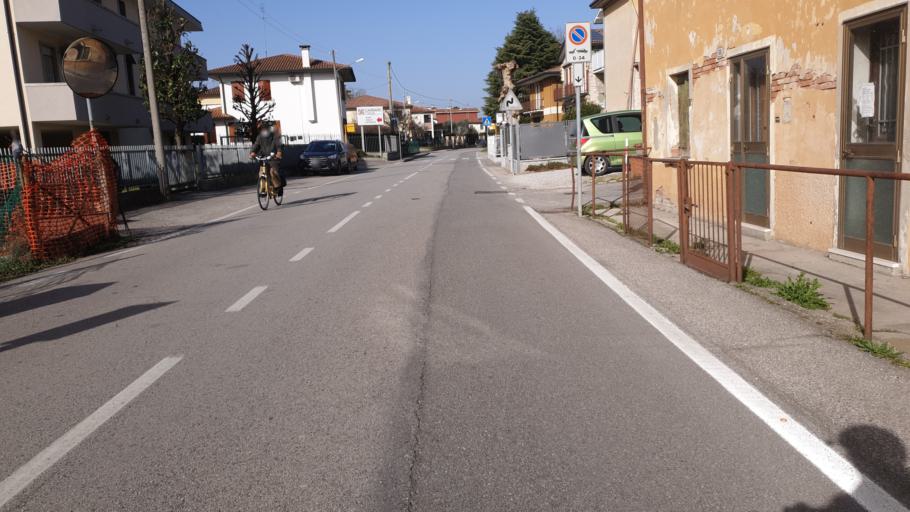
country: IT
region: Veneto
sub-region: Provincia di Padova
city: Cadoneghe
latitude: 45.4315
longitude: 11.9369
